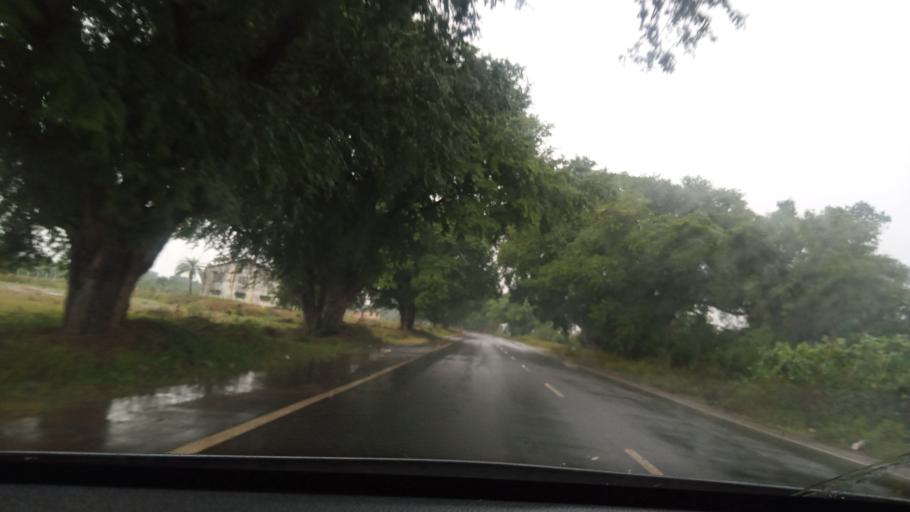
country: IN
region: Tamil Nadu
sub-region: Vellore
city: Kalavai
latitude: 12.8048
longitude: 79.4256
